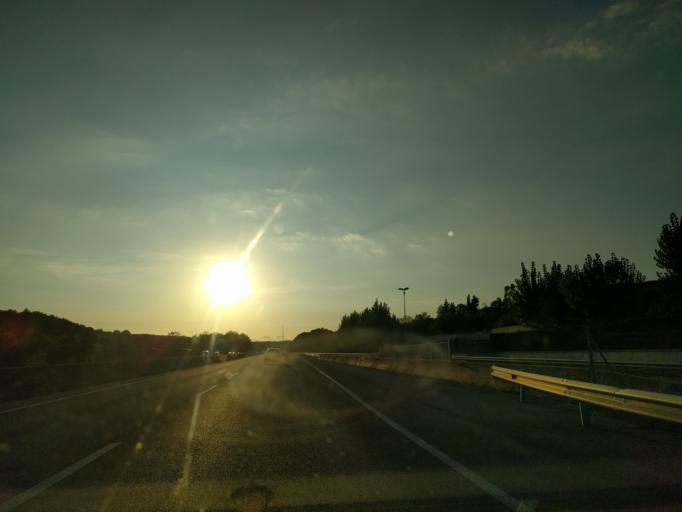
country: ES
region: Catalonia
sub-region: Provincia de Girona
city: Santa Cristina d'Aro
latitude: 41.8275
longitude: 2.9591
